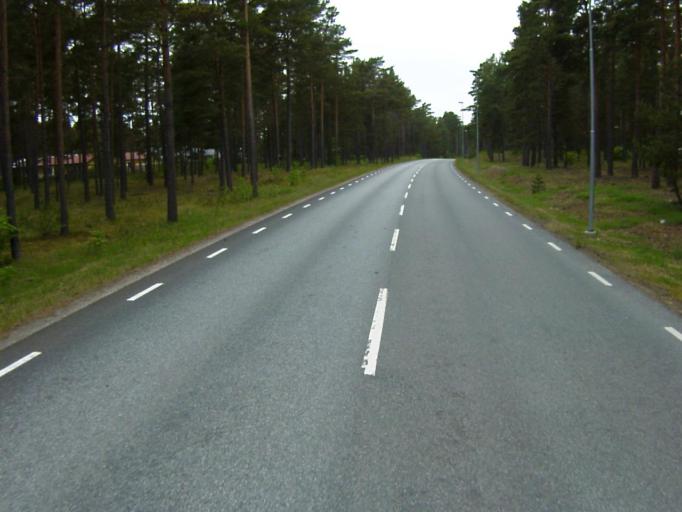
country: SE
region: Skane
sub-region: Kristianstads Kommun
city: Ahus
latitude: 55.9412
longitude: 14.3108
